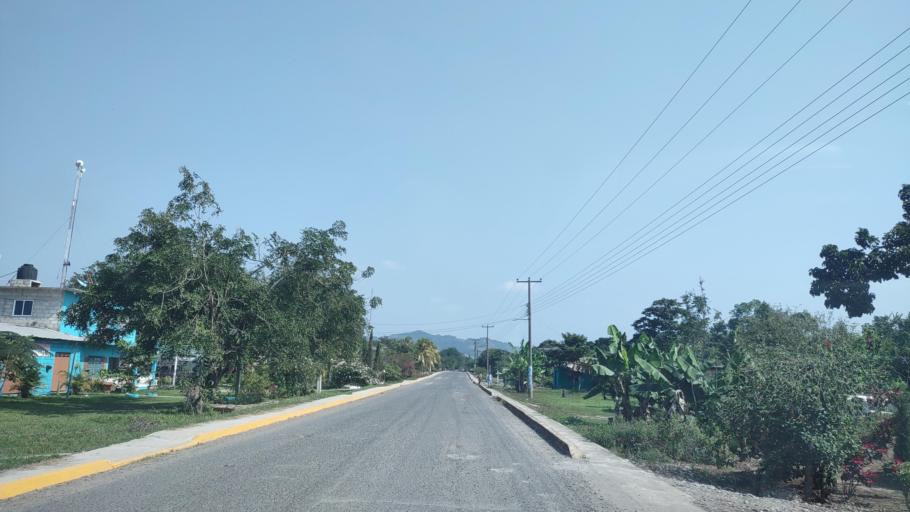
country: MX
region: Puebla
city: Espinal
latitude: 20.2617
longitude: -97.3129
